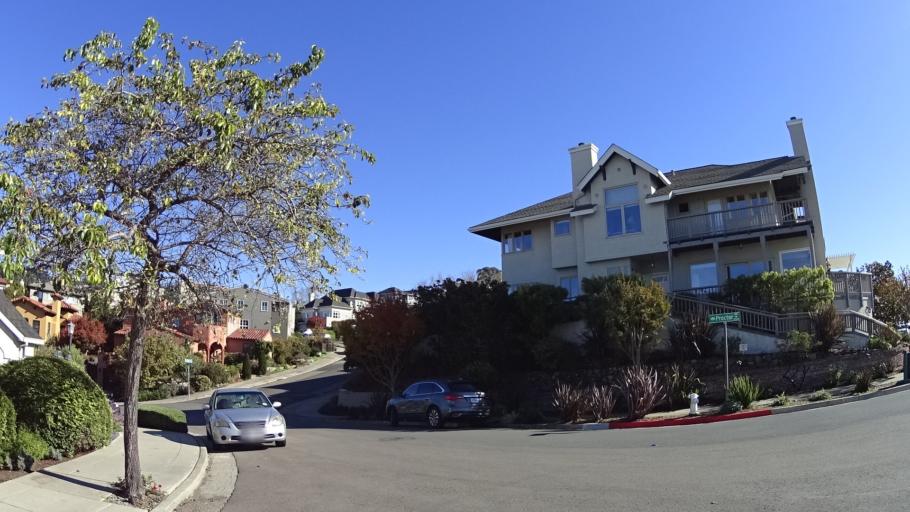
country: US
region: California
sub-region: Alameda County
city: Piedmont
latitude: 37.8407
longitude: -122.2277
